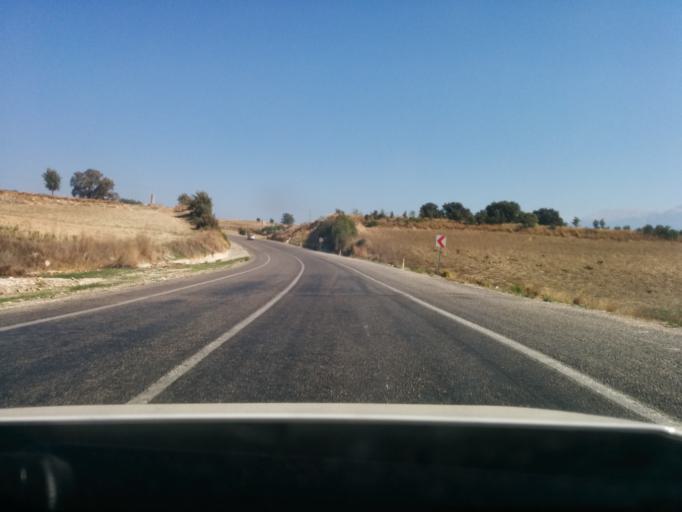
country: TR
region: Mugla
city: Esen
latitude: 36.4463
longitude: 29.2902
